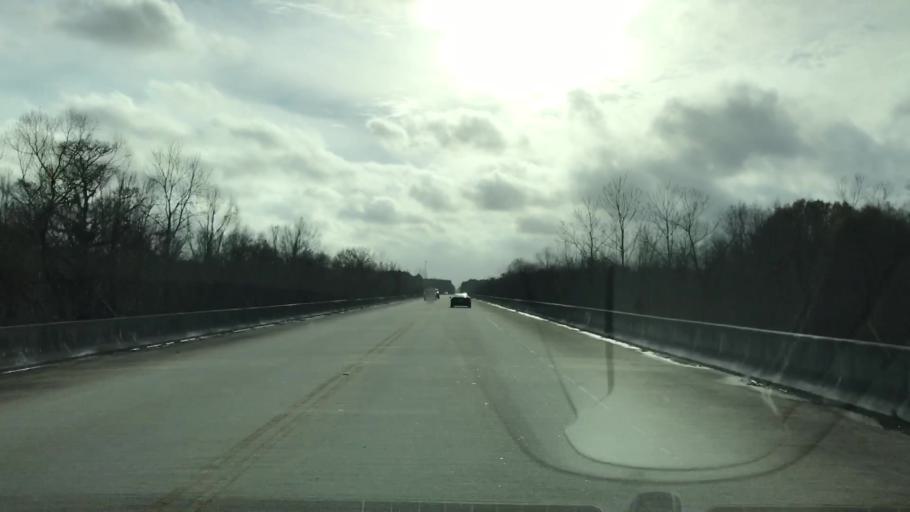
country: US
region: South Carolina
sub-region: Williamsburg County
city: Andrews
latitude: 33.3085
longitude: -79.6749
